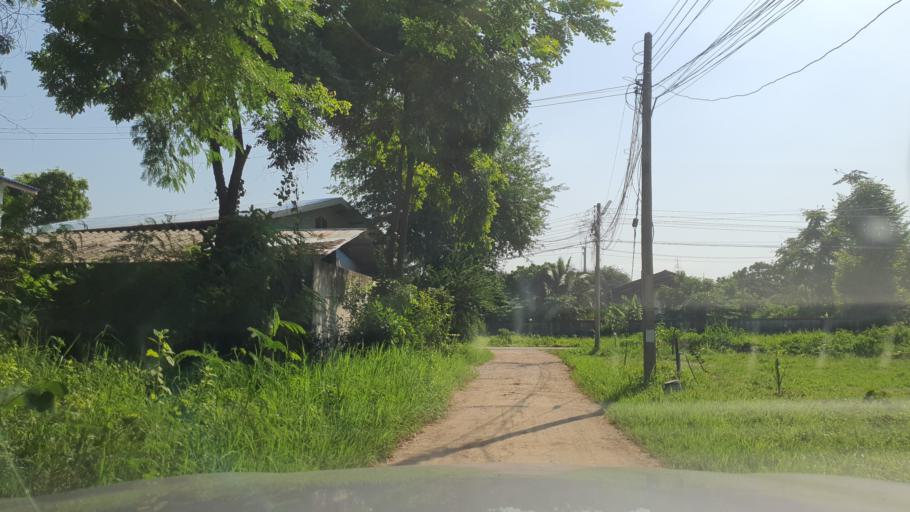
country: TH
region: Chiang Mai
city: Hang Dong
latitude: 18.7204
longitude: 98.9307
